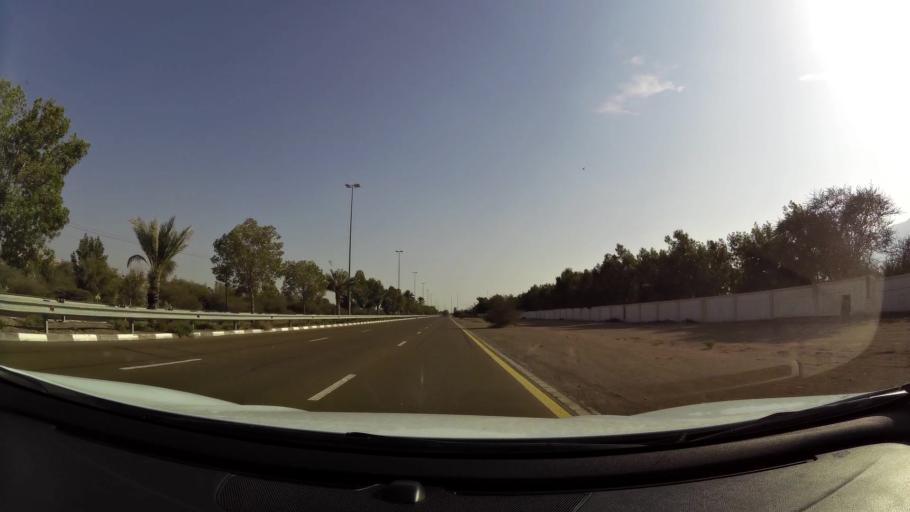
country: AE
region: Abu Dhabi
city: Al Ain
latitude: 24.0502
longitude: 55.8409
